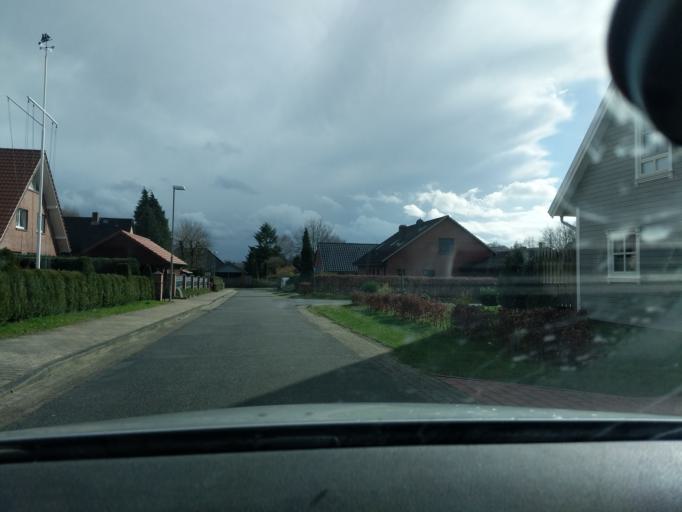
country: DE
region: Lower Saxony
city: Oldendorf
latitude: 53.5866
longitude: 9.2431
